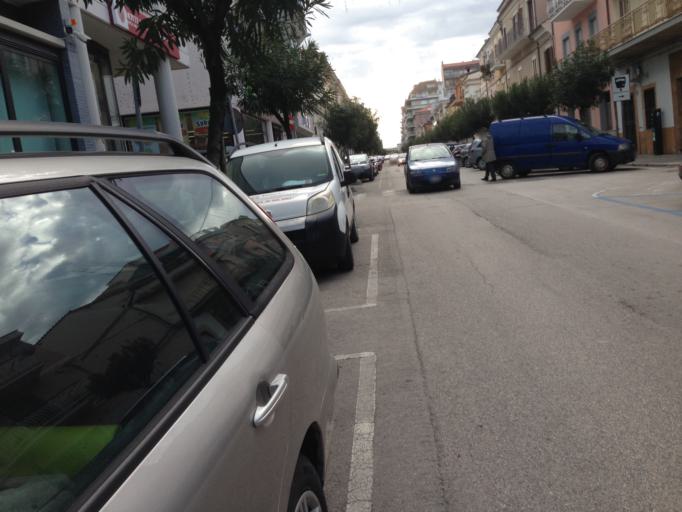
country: IT
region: Molise
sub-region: Provincia di Campobasso
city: Termoli
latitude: 42.0020
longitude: 14.9968
